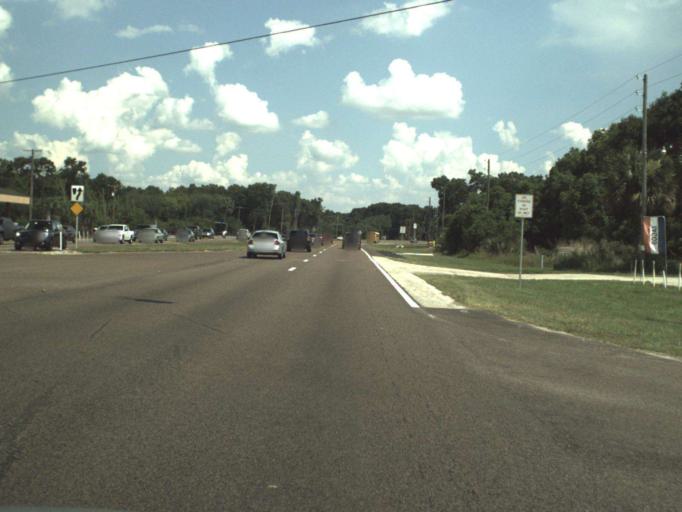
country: US
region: Florida
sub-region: Lake County
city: Mount Dora
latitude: 28.8152
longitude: -81.6290
